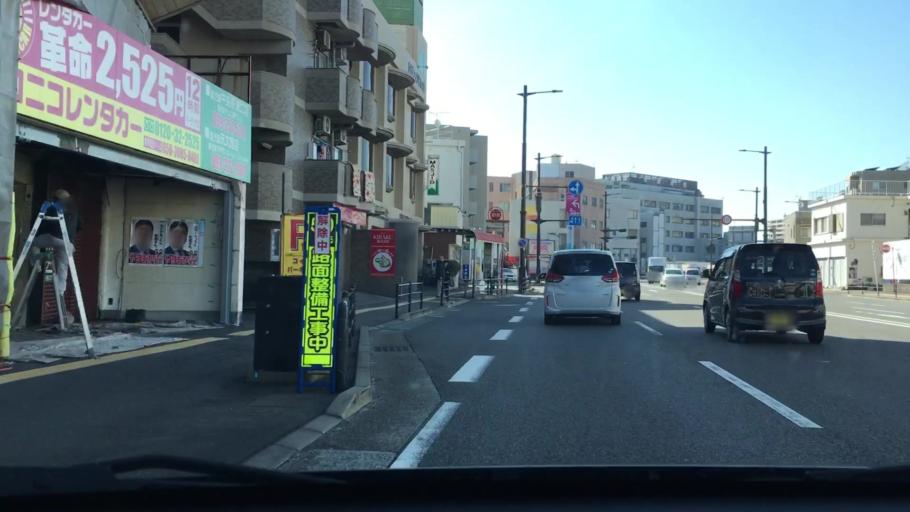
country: JP
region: Kagoshima
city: Kagoshima-shi
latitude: 31.5593
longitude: 130.5496
